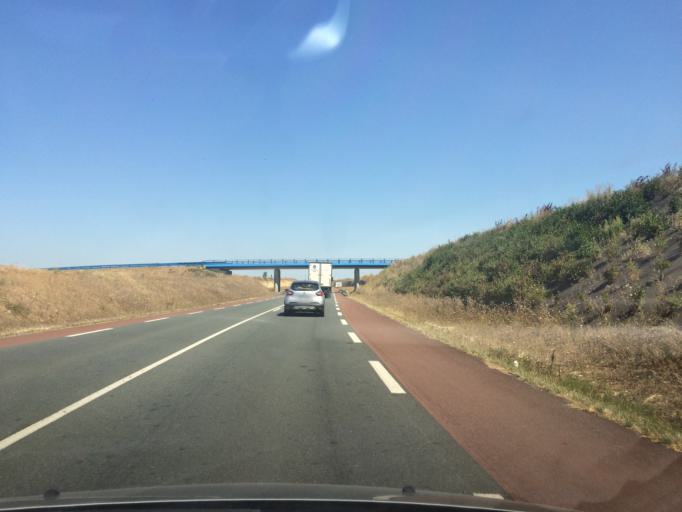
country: FR
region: Poitou-Charentes
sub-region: Departement de la Charente-Maritime
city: Esnandes
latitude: 46.2371
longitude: -1.0777
